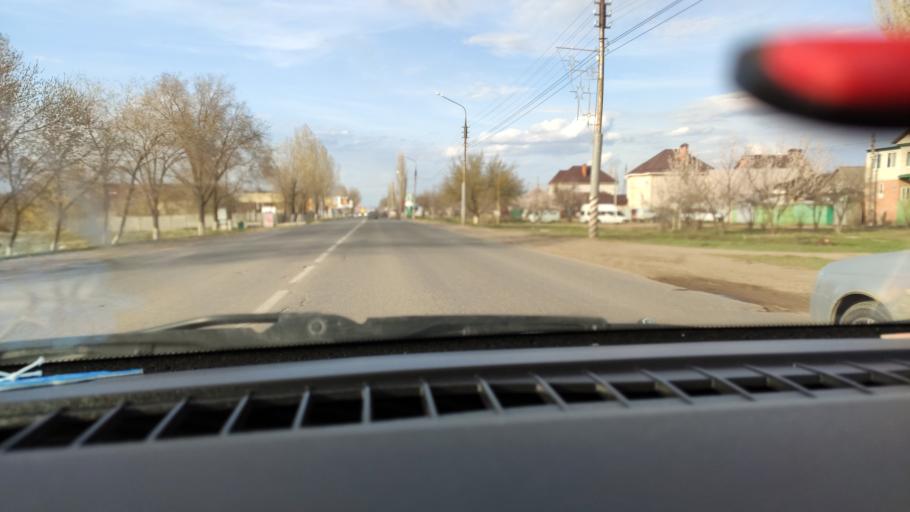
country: RU
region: Saratov
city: Engel's
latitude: 51.4604
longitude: 46.0911
